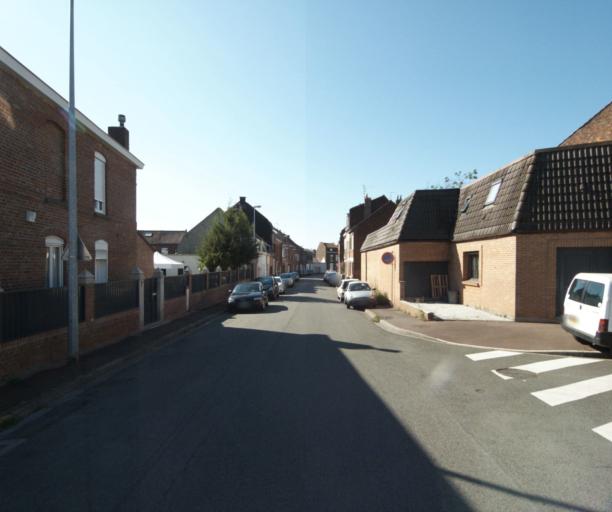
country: FR
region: Nord-Pas-de-Calais
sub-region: Departement du Nord
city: Mouvaux
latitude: 50.7037
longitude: 3.1527
